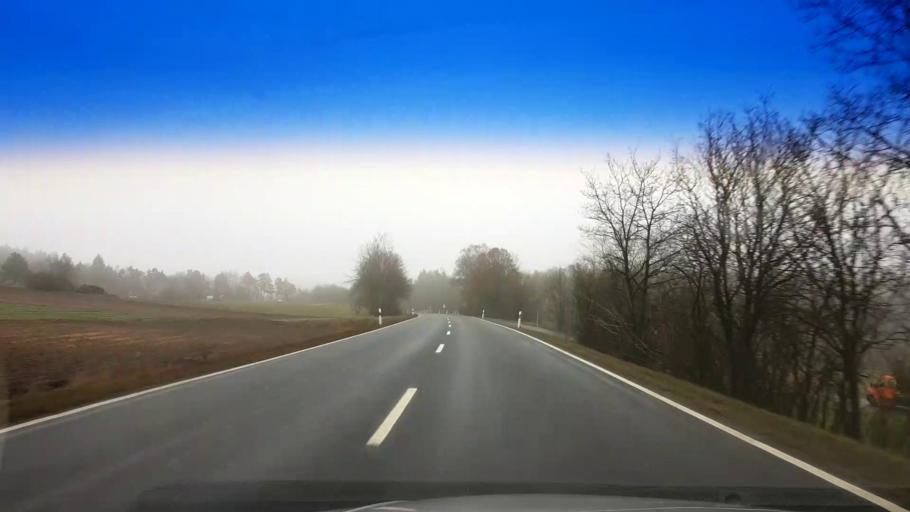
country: DE
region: Bavaria
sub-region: Upper Palatinate
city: Wiesau
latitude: 49.8599
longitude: 12.2005
